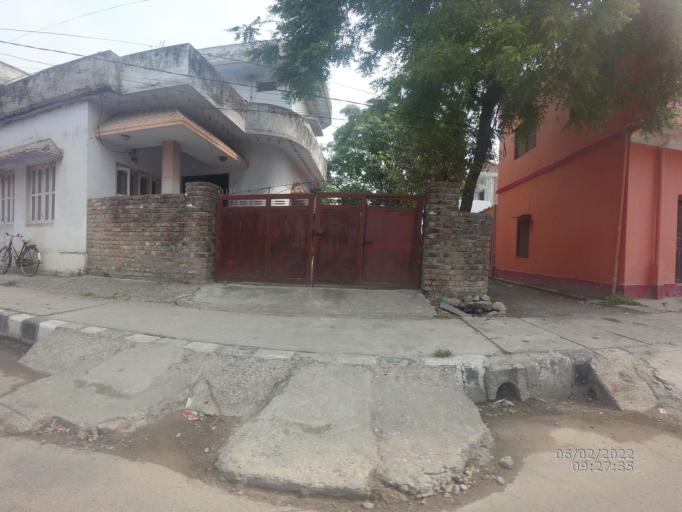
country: NP
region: Western Region
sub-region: Lumbini Zone
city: Bhairahawa
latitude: 27.5008
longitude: 83.4494
